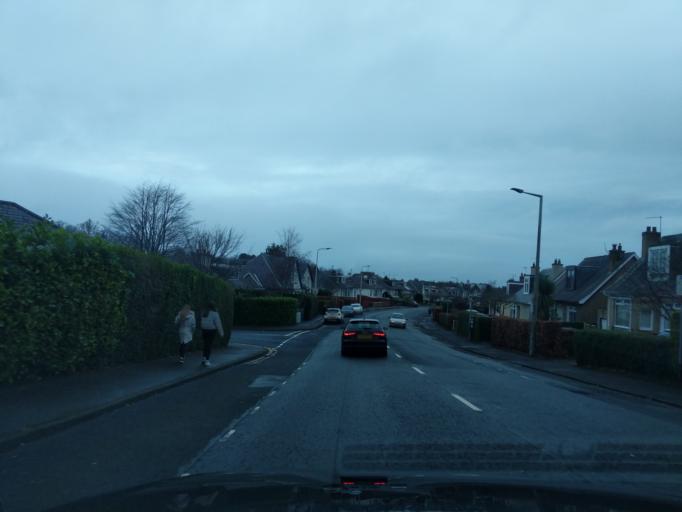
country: GB
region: Scotland
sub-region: Edinburgh
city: Edinburgh
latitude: 55.9550
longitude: -3.2332
